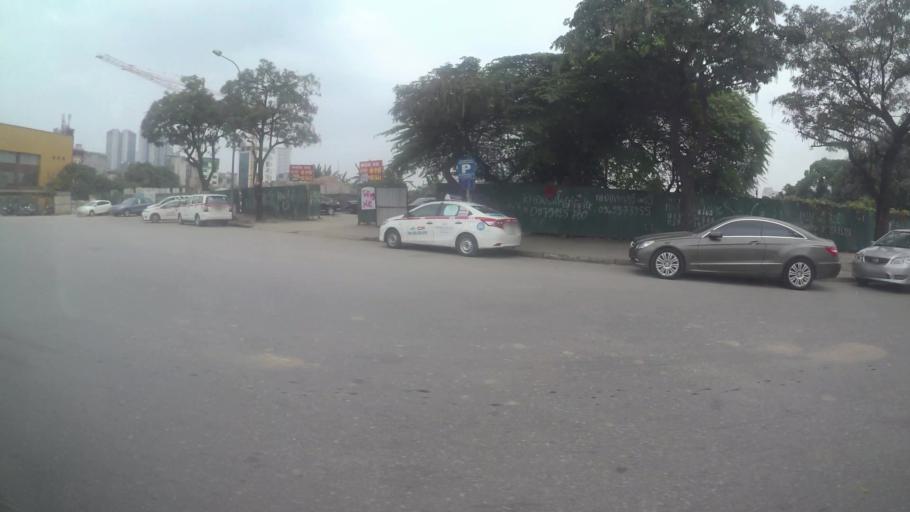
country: VN
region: Ha Noi
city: Cau Dien
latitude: 21.0276
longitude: 105.7686
